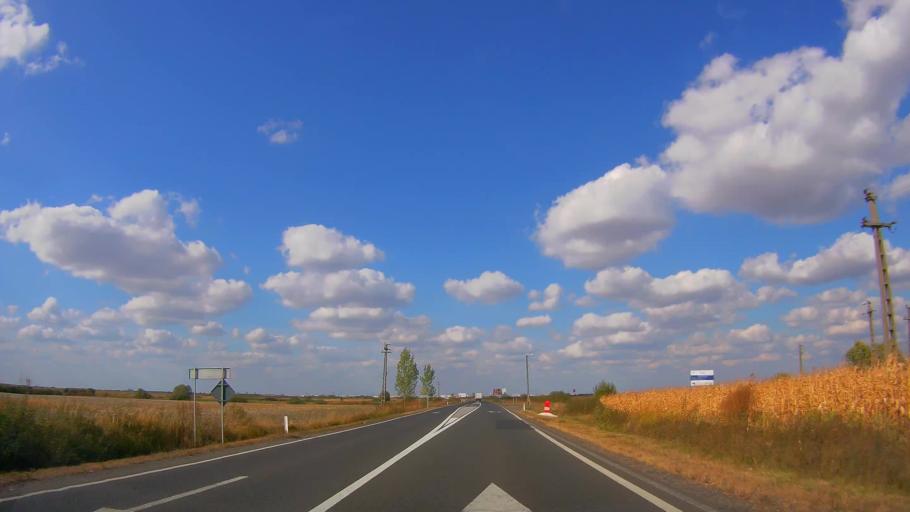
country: RO
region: Satu Mare
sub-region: Oras Ardud
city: Madaras
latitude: 47.7072
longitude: 22.8724
